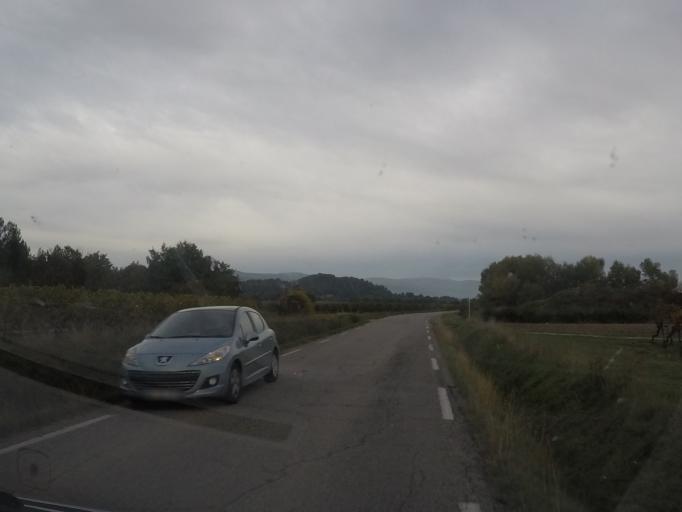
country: FR
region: Provence-Alpes-Cote d'Azur
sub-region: Departement du Vaucluse
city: Roussillon
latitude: 43.9161
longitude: 5.2631
